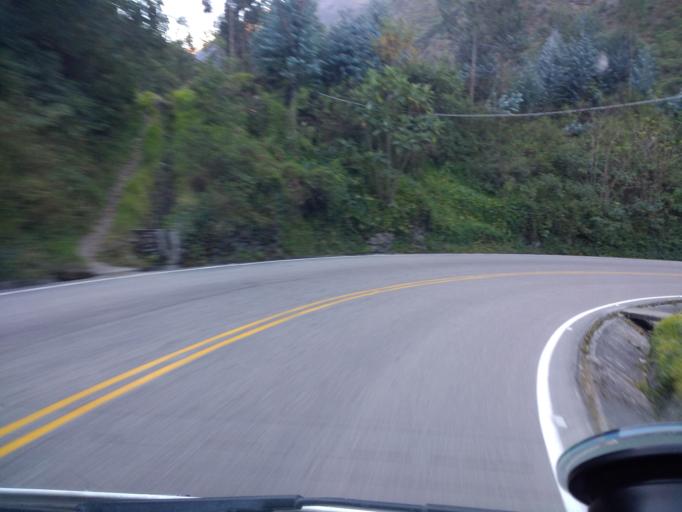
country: PE
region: Cusco
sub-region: Provincia de Urubamba
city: Ollantaytambo
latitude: -13.2015
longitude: -72.2962
